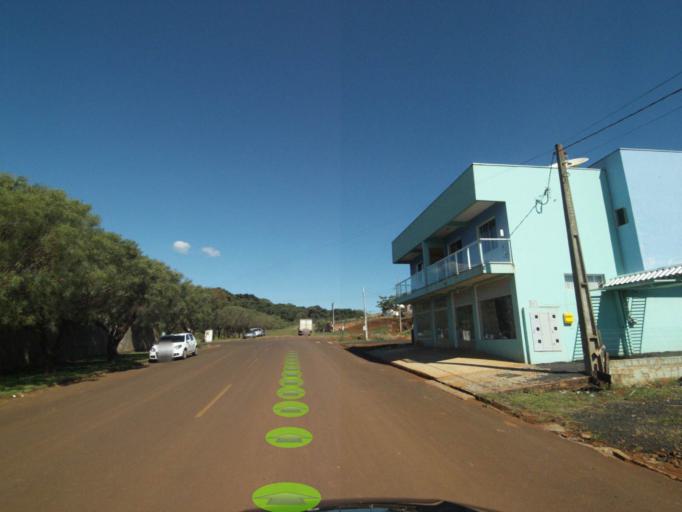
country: BR
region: Parana
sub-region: Coronel Vivida
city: Coronel Vivida
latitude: -26.1459
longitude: -52.3811
